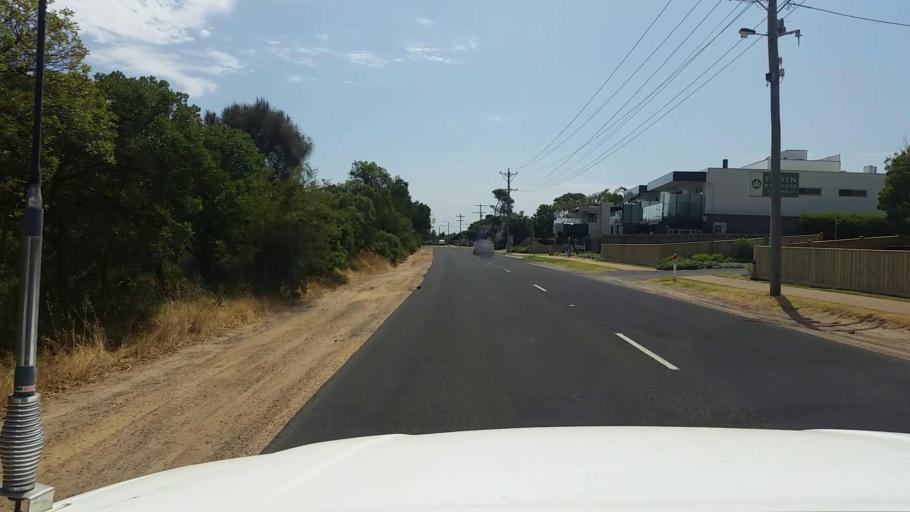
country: AU
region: Victoria
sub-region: Mornington Peninsula
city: Mount Martha
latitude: -38.2462
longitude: 145.0296
